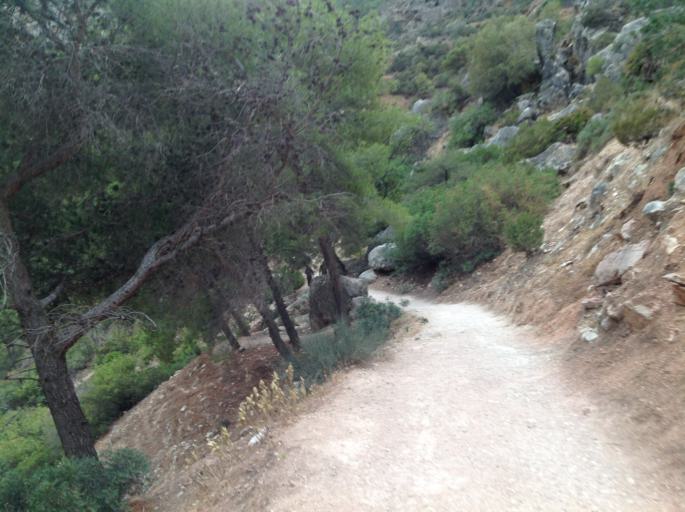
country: ES
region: Andalusia
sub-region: Provincia de Malaga
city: Ardales
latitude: 36.9261
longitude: -4.7824
